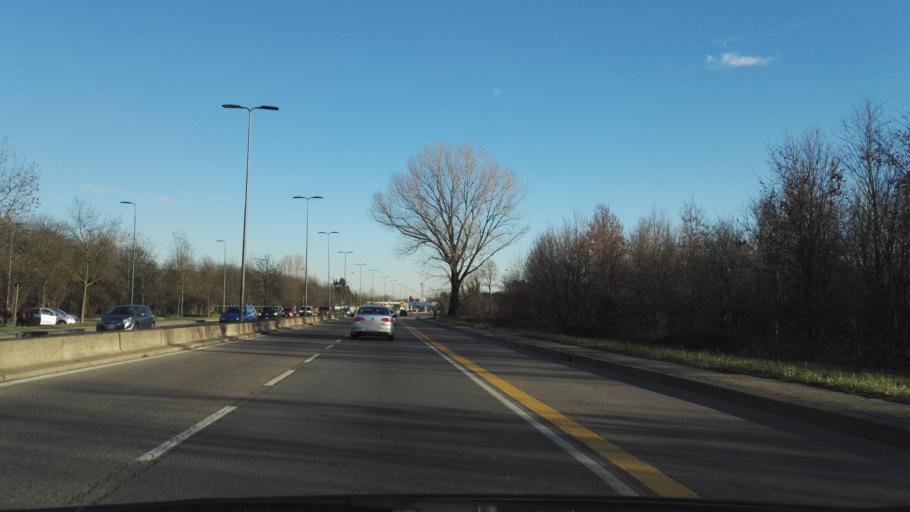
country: IT
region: Lombardy
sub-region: Citta metropolitana di Milano
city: Figino
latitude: 45.4815
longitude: 9.0956
